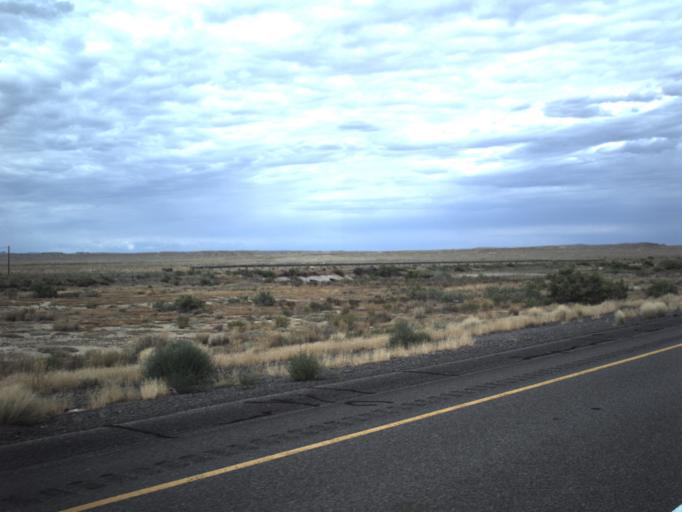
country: US
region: Utah
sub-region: Grand County
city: Moab
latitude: 38.9418
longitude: -109.5643
